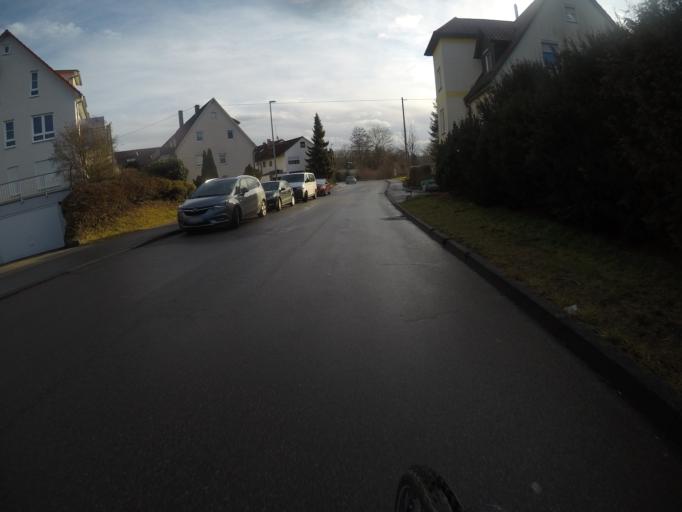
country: DE
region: Baden-Wuerttemberg
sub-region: Regierungsbezirk Stuttgart
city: Unterensingen
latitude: 48.6526
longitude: 9.3509
